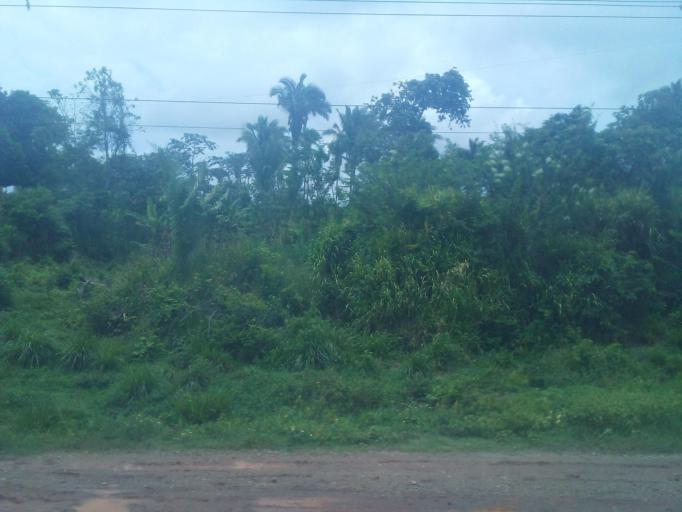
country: BR
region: Maranhao
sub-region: Vitoria Do Mearim
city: Vitoria do Mearim
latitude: -3.5955
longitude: -44.9888
